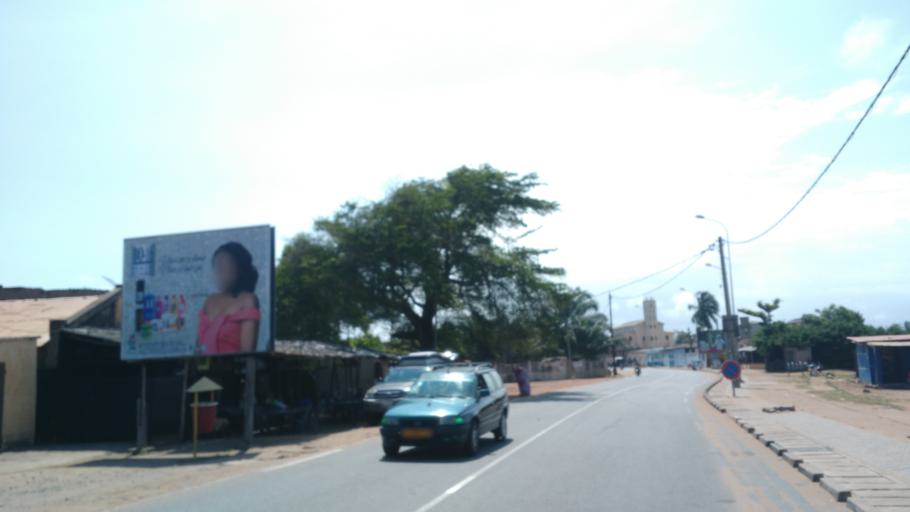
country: TG
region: Maritime
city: Aneho
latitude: 6.2275
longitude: 1.5930
